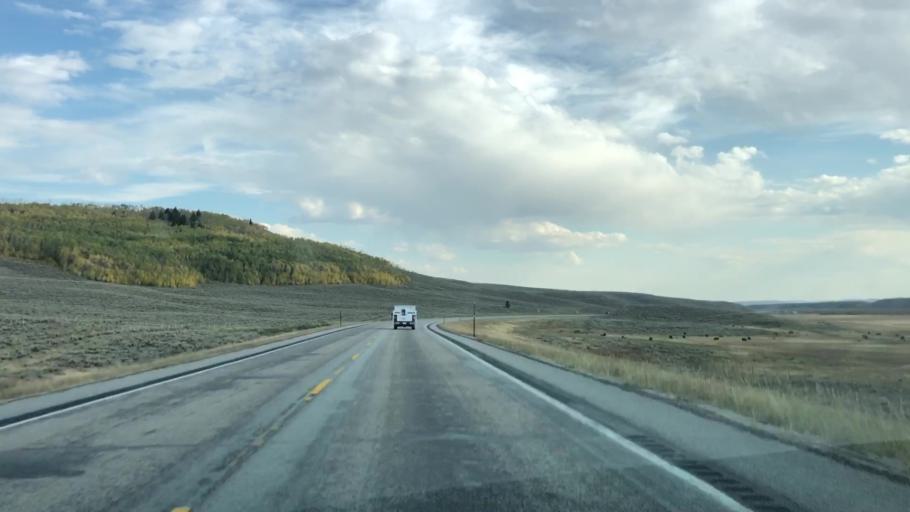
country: US
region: Wyoming
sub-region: Sublette County
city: Pinedale
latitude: 43.0881
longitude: -110.1637
